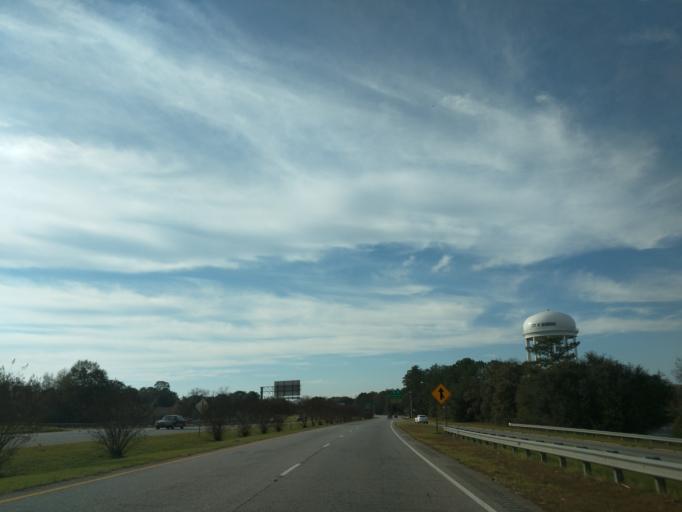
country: US
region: Georgia
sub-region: Decatur County
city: Bainbridge
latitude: 30.8909
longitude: -84.5679
